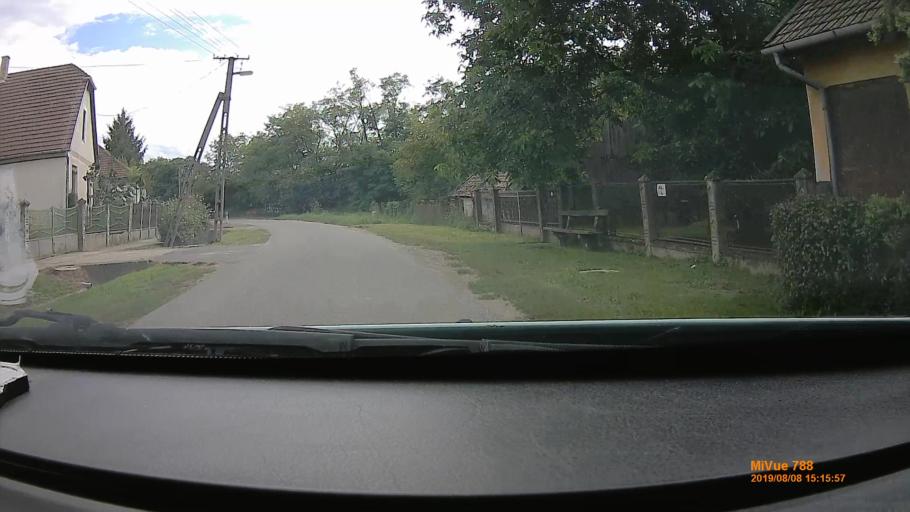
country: HU
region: Szabolcs-Szatmar-Bereg
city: Tunyogmatolcs
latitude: 47.9663
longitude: 22.4579
